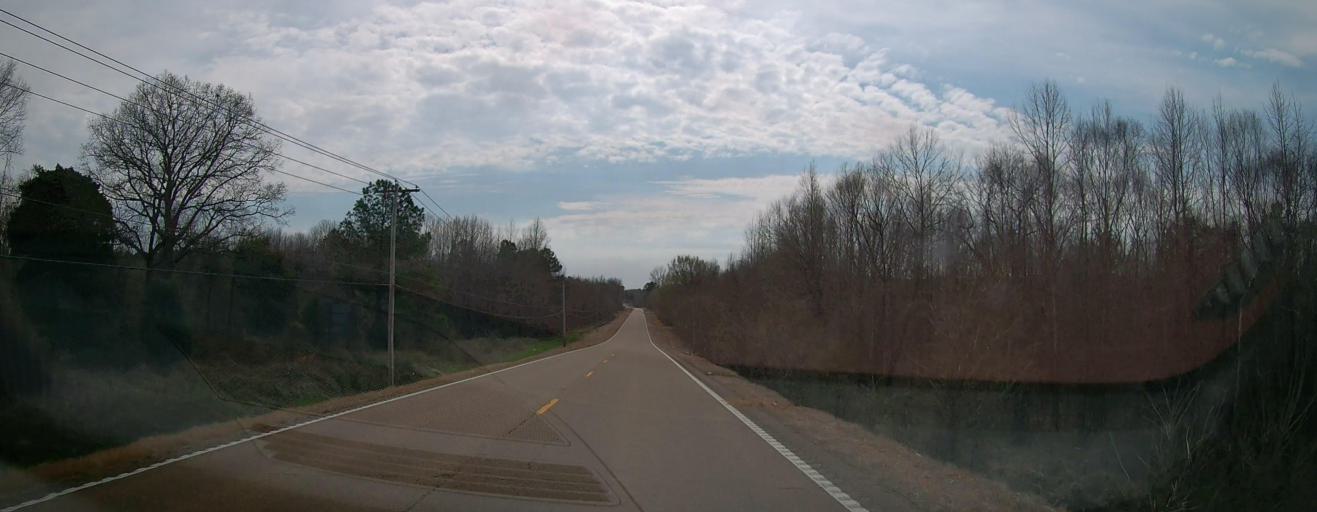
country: US
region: Mississippi
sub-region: Marshall County
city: Holly Springs
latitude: 34.7332
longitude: -89.4212
